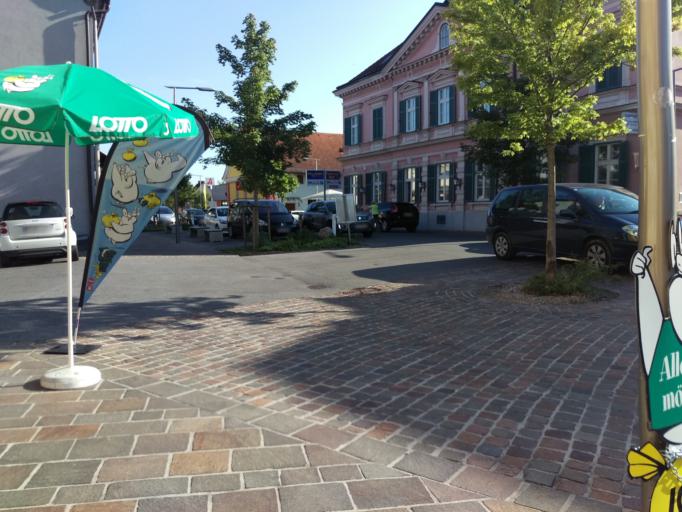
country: AT
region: Styria
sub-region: Politischer Bezirk Graz-Umgebung
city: Feldkirchen bei Graz
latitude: 47.0125
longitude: 15.4434
